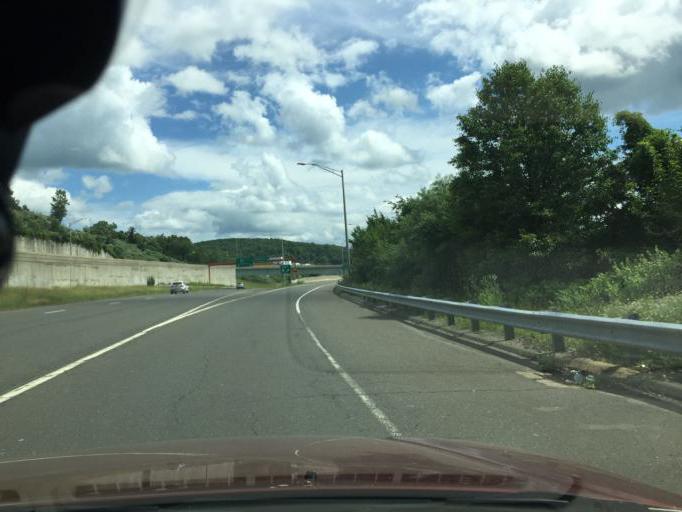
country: US
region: Connecticut
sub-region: Fairfield County
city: Danbury
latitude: 41.3797
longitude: -73.4745
